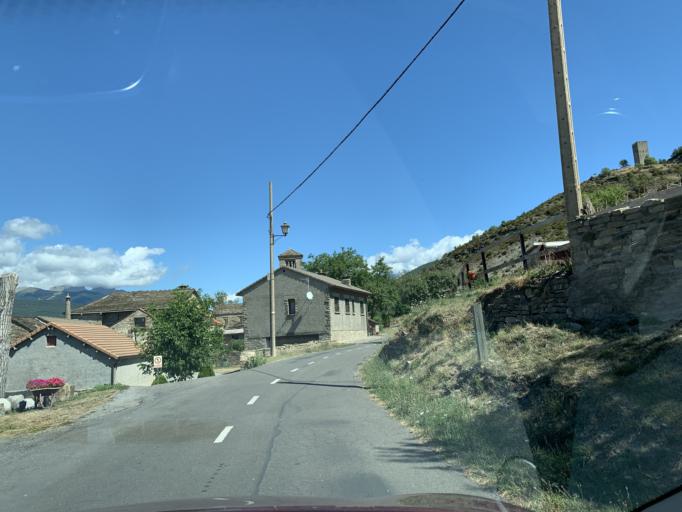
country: ES
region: Aragon
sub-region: Provincia de Huesca
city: Sabinanigo
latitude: 42.5534
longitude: -0.3180
